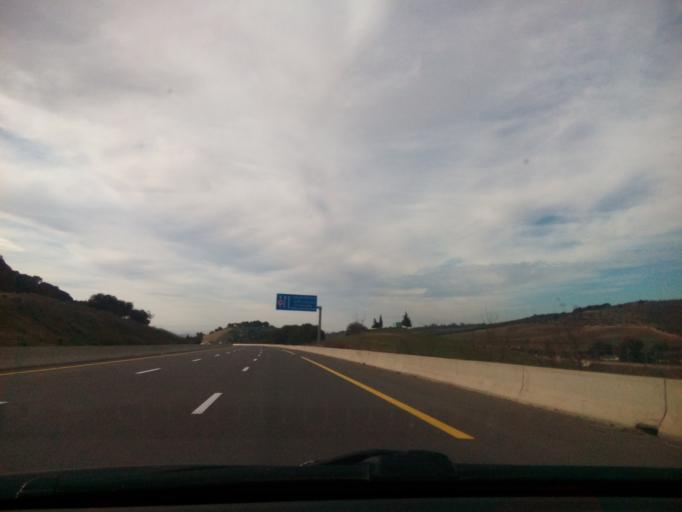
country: DZ
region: Sidi Bel Abbes
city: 'Ain el Berd
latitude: 35.3581
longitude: -0.5089
